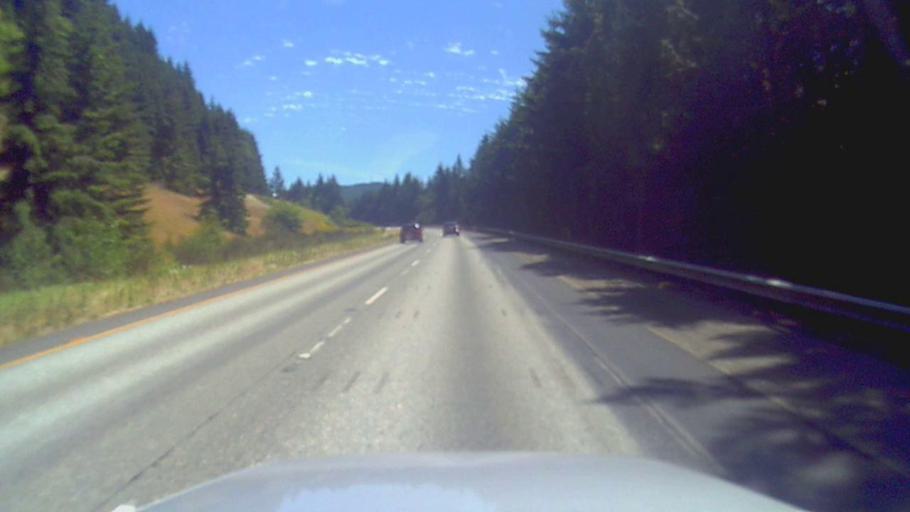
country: US
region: Washington
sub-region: Whatcom County
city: Geneva
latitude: 48.6939
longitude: -122.4522
